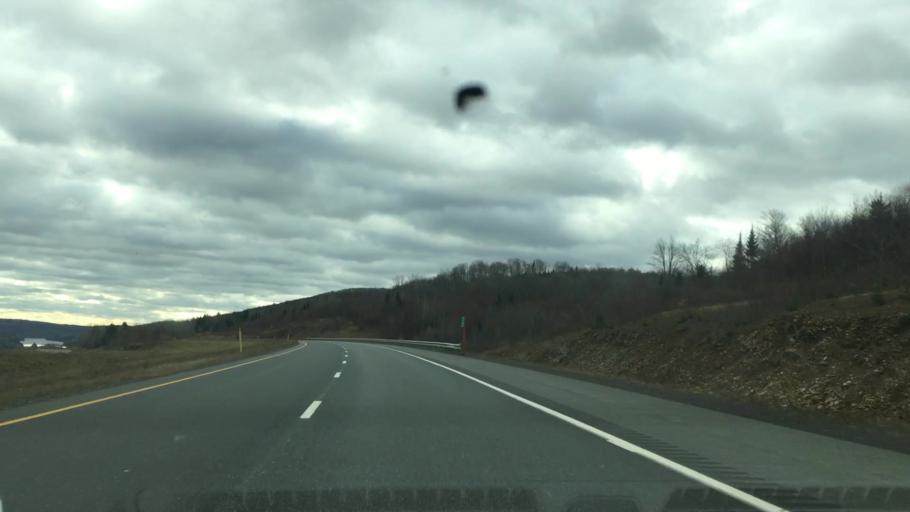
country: US
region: Maine
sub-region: Aroostook County
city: Fort Fairfield
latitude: 46.6978
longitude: -67.7421
